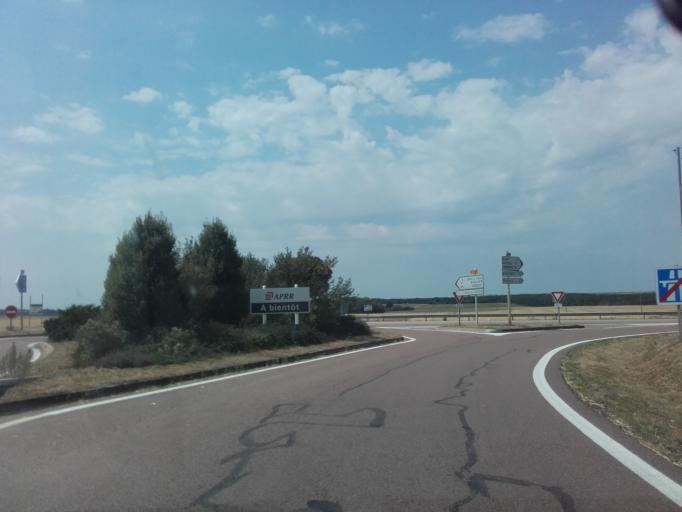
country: FR
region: Bourgogne
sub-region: Departement de l'Yonne
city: Joux-la-Ville
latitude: 47.6592
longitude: 3.8777
